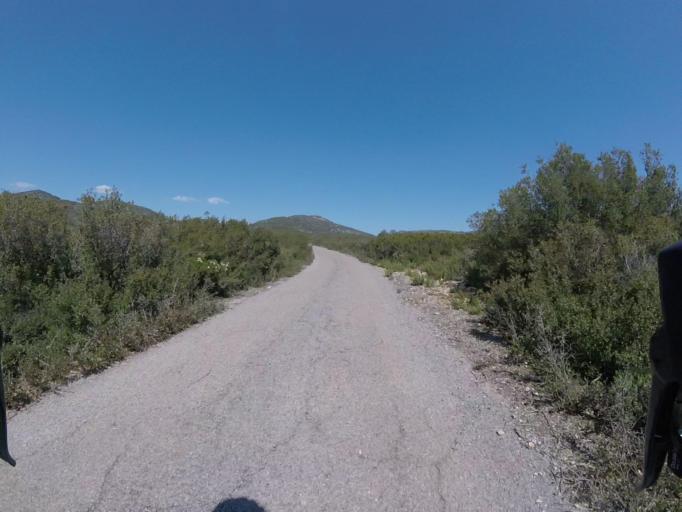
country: ES
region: Valencia
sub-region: Provincia de Castello
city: Sierra-Engarceran
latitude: 40.2427
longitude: -0.0265
